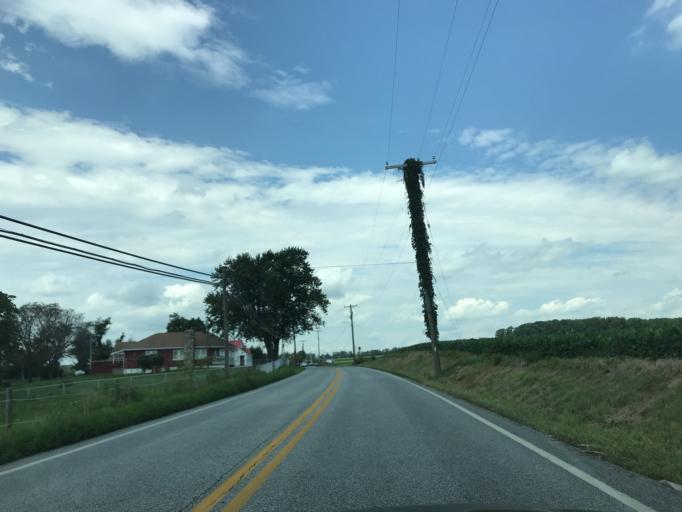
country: US
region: Pennsylvania
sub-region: York County
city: New Freedom
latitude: 39.6850
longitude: -76.7338
